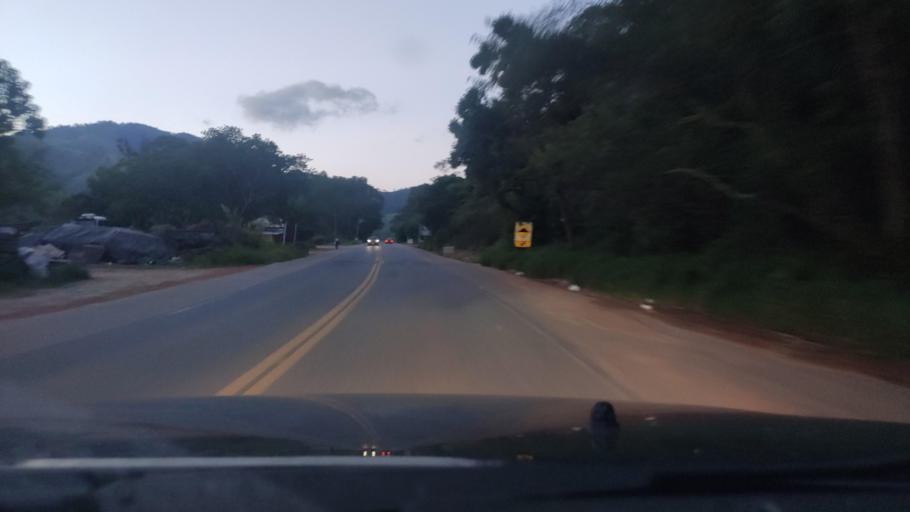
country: BR
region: Sao Paulo
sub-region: Campos Do Jordao
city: Campos do Jordao
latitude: -22.7418
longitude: -45.7392
